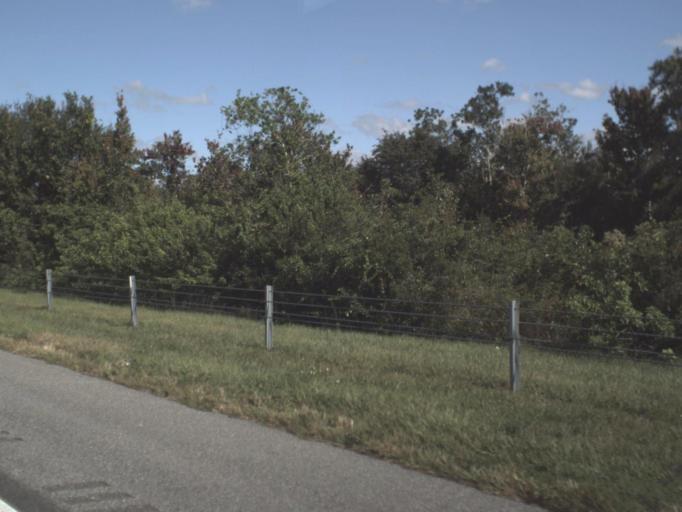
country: US
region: Florida
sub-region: Osceola County
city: Saint Cloud
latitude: 28.1085
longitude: -81.2808
